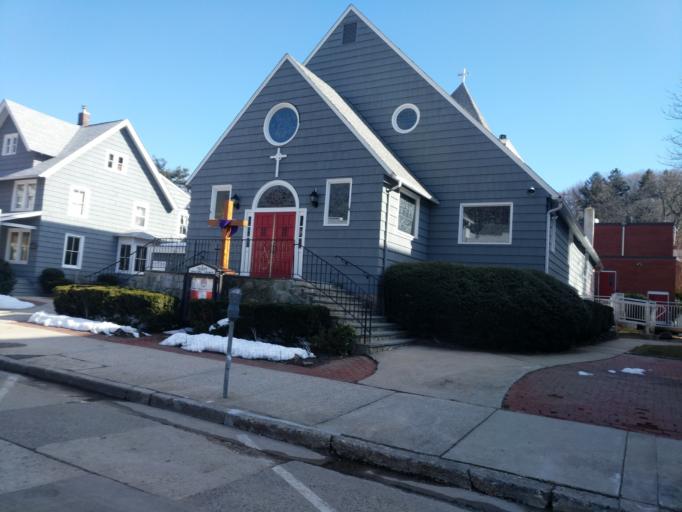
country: US
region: New York
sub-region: Suffolk County
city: Northport
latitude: 40.9004
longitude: -73.3498
